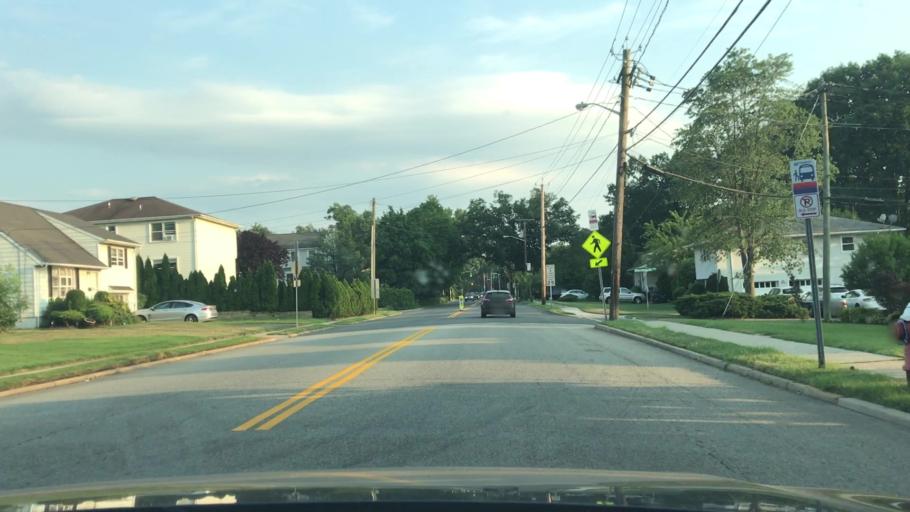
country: US
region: New Jersey
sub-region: Bergen County
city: New Milford
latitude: 40.9330
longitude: -74.0170
